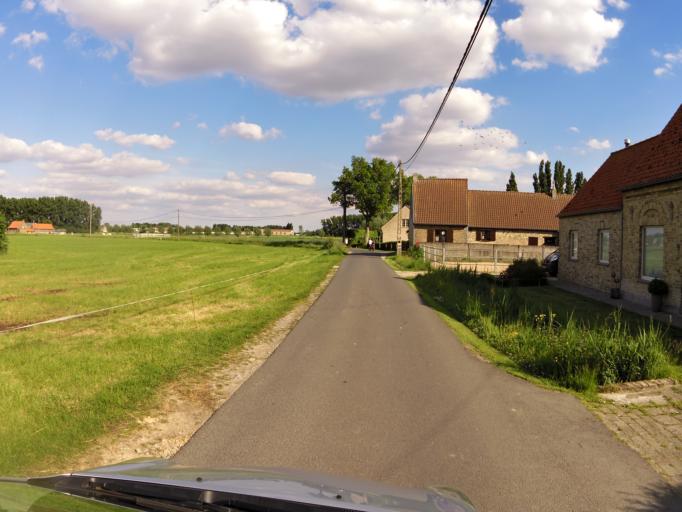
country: BE
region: Flanders
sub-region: Provincie West-Vlaanderen
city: Diksmuide
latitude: 50.9981
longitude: 2.8514
